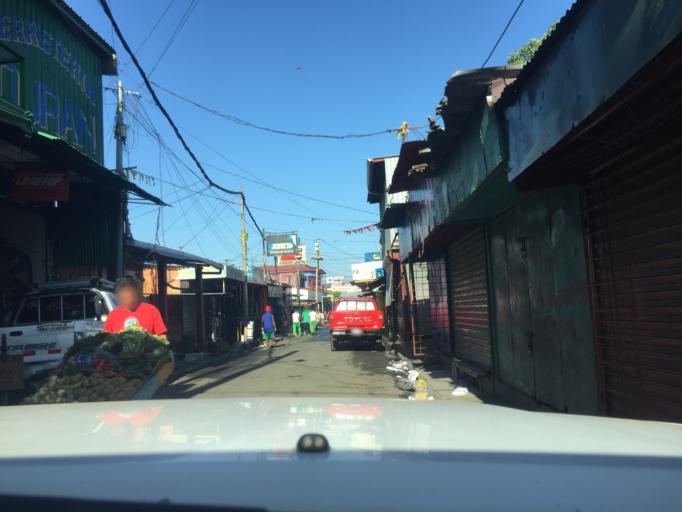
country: NI
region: Managua
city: Managua
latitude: 12.1513
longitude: -86.2591
